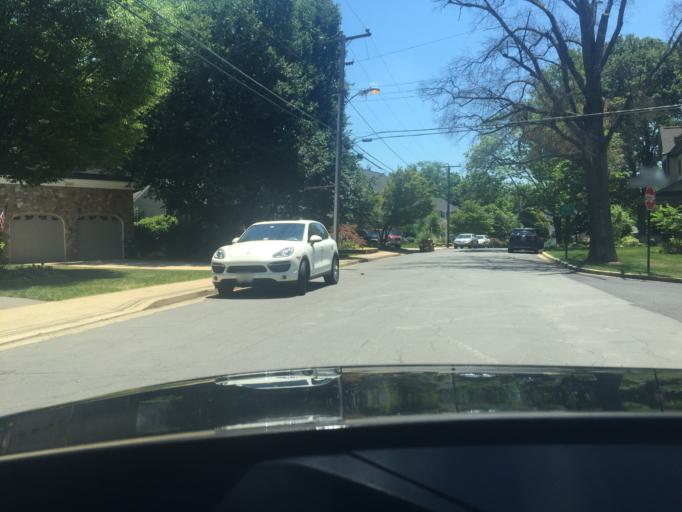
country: US
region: Virginia
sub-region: Arlington County
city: Arlington
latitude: 38.9093
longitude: -77.1100
